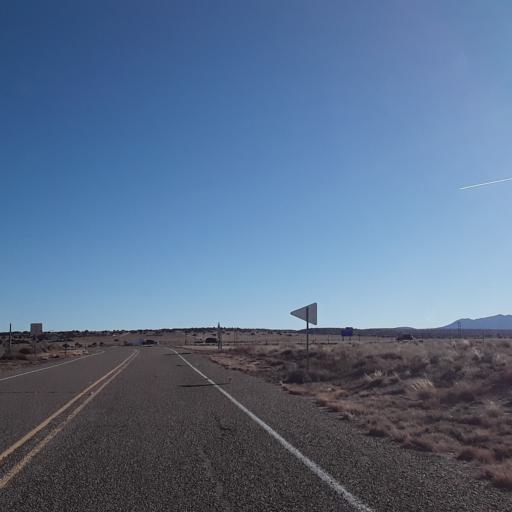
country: US
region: New Mexico
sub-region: Sandoval County
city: Santo Domingo Pueblo
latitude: 35.4532
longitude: -106.3495
